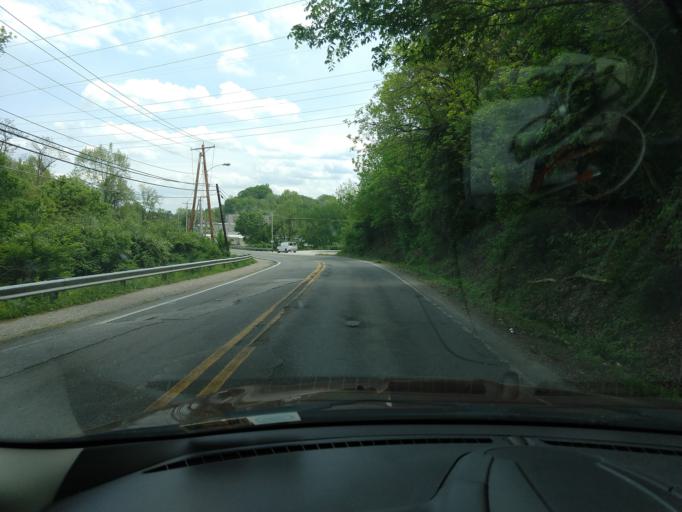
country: US
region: West Virginia
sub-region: Kanawha County
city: Saint Albans
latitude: 38.3755
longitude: -81.7963
